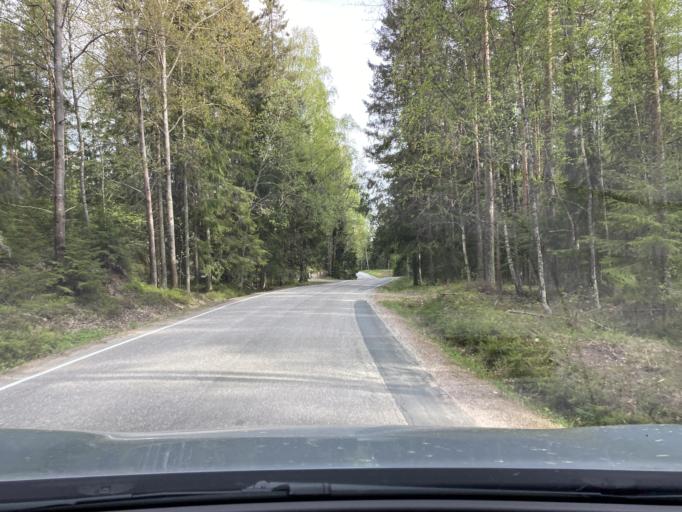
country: FI
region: Varsinais-Suomi
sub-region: Salo
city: Kiikala
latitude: 60.4747
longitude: 23.5333
